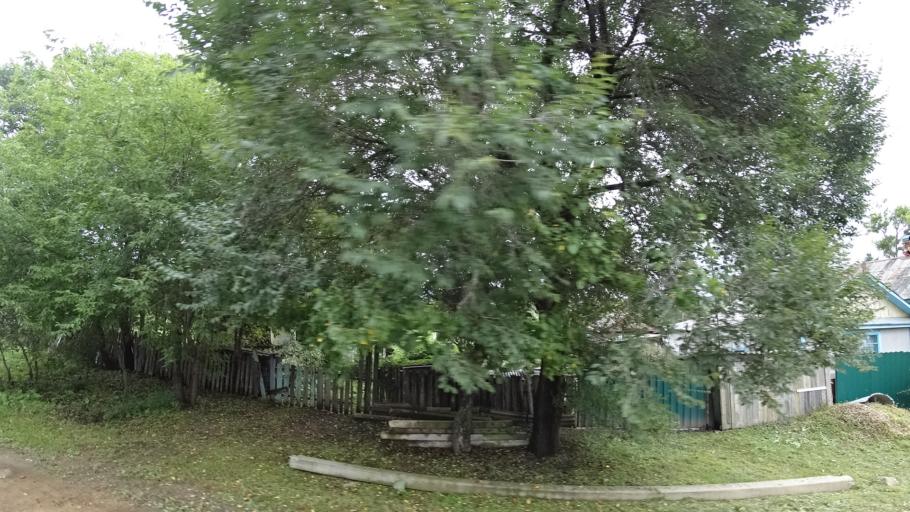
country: RU
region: Primorskiy
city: Rettikhovka
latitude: 44.1700
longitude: 132.7671
